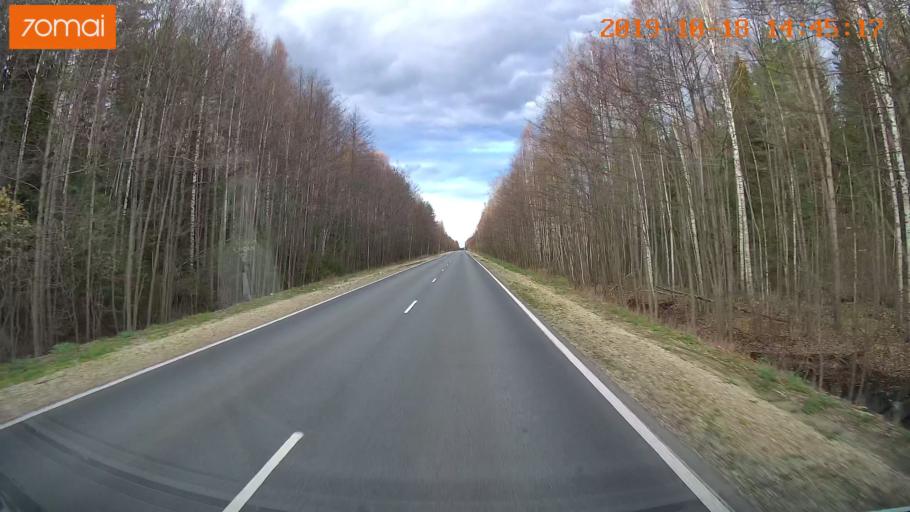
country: RU
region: Vladimir
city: Velikodvorskiy
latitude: 55.3523
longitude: 40.6786
